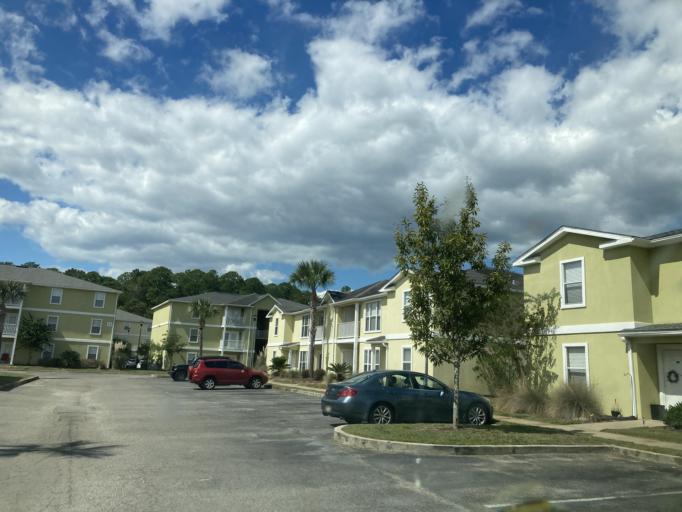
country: US
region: Mississippi
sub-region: Jackson County
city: Saint Martin
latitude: 30.4459
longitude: -88.8524
